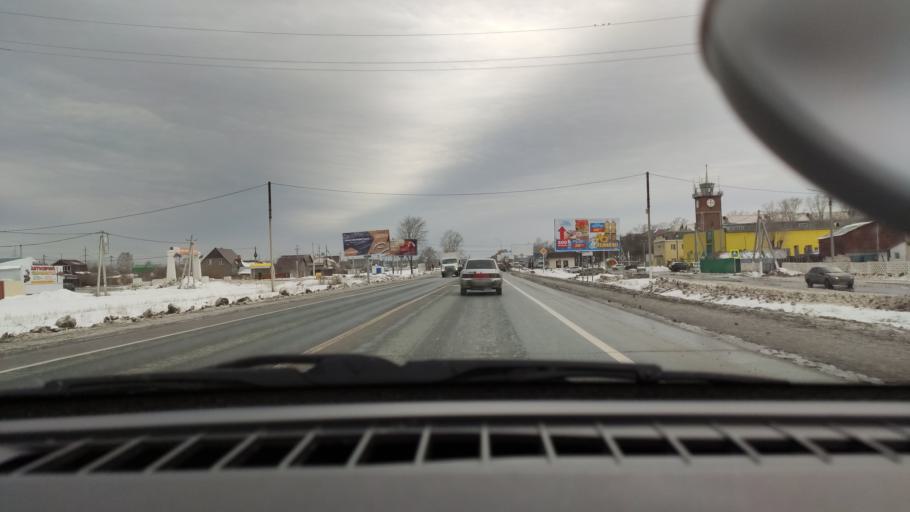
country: RU
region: Samara
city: Kurumoch
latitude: 53.4838
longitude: 50.0314
